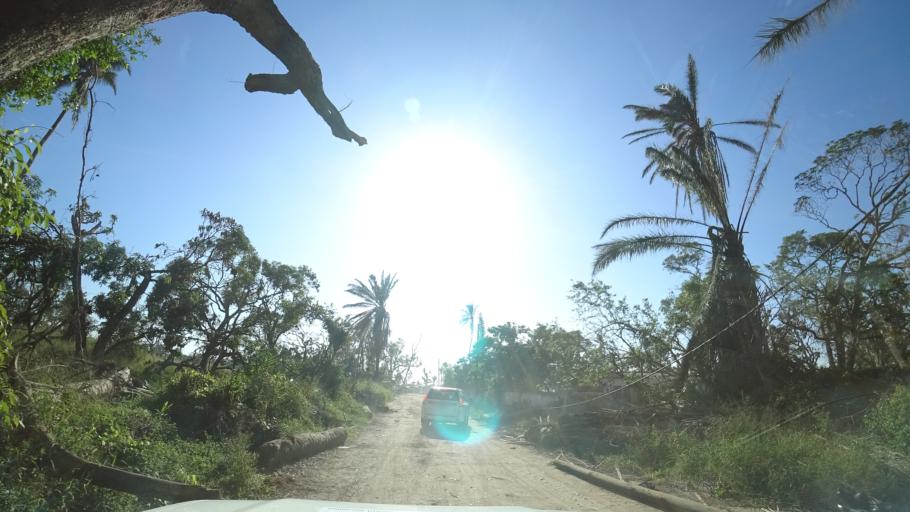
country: MZ
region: Sofala
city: Beira
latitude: -19.7652
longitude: 34.8963
